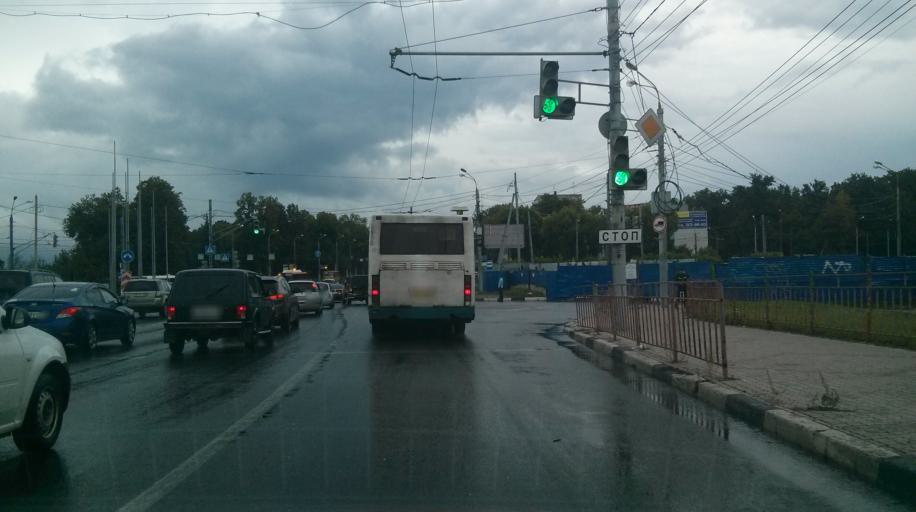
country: RU
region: Nizjnij Novgorod
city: Nizhniy Novgorod
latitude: 56.2553
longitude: 43.9708
